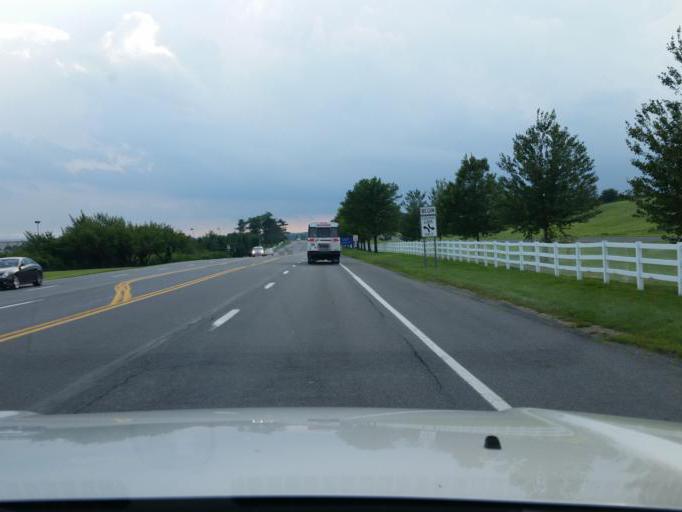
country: US
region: Pennsylvania
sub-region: Dauphin County
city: Hershey
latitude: 40.2928
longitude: -76.6596
